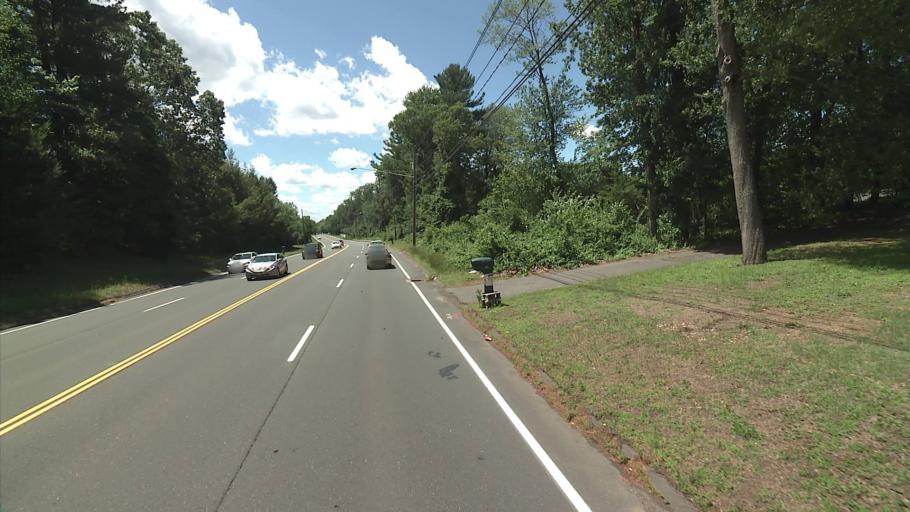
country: US
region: Connecticut
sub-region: Hartford County
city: Sherwood Manor
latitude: 42.0075
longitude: -72.5516
